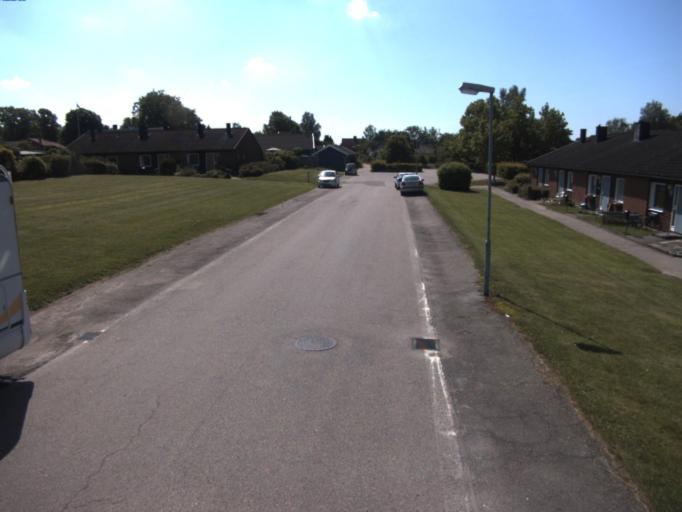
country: SE
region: Skane
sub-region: Helsingborg
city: Barslov
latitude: 56.0341
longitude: 12.8205
